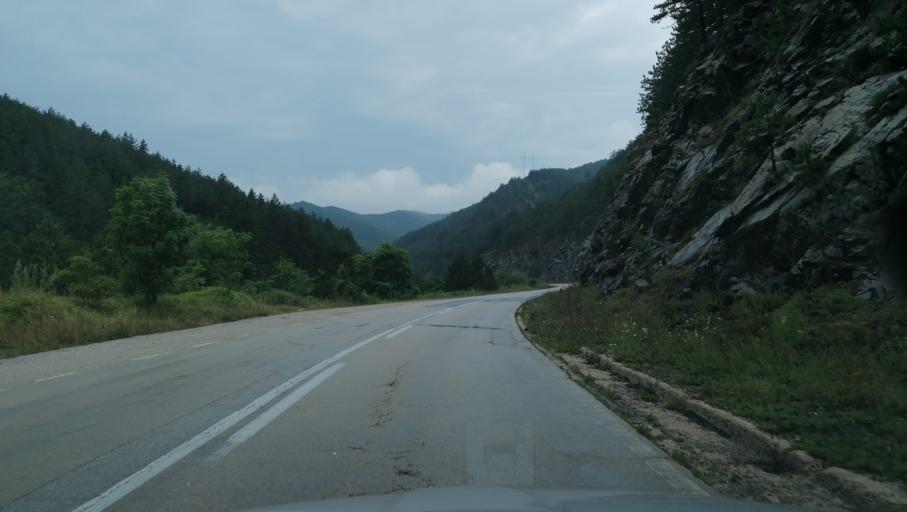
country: RS
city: Durici
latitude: 43.8307
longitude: 19.5334
